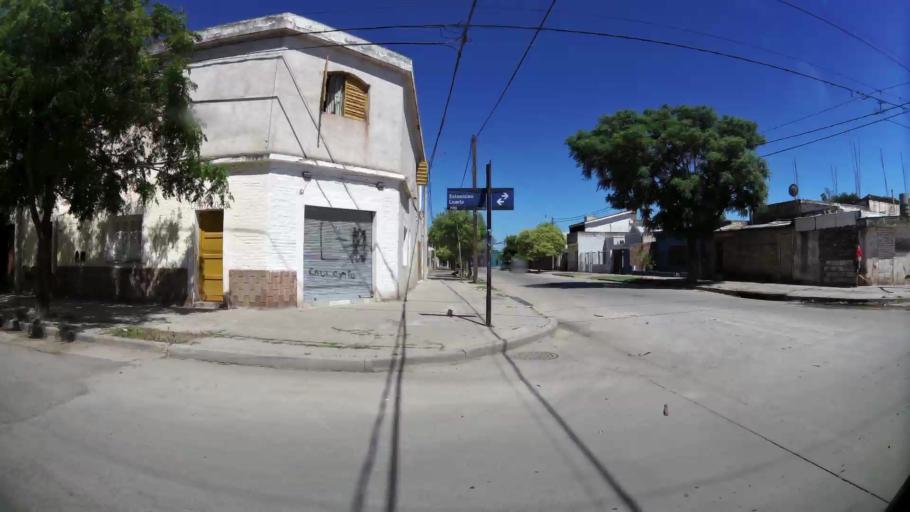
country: AR
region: Cordoba
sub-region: Departamento de Capital
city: Cordoba
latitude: -31.4168
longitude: -64.1370
